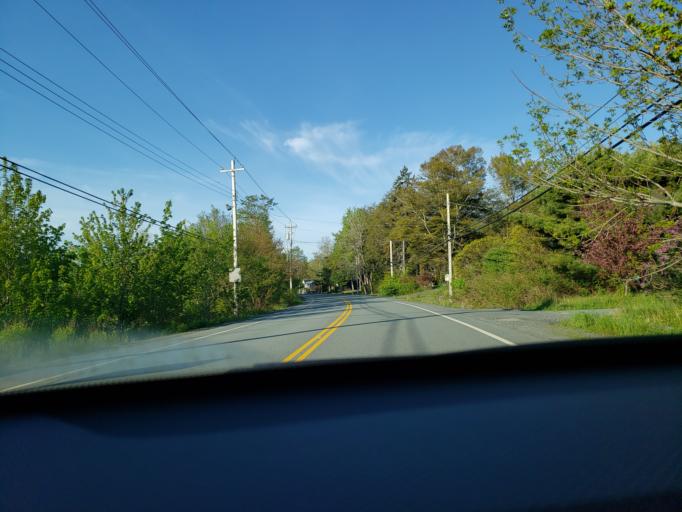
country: CA
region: Nova Scotia
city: Cole Harbour
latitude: 44.7390
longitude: -63.3869
